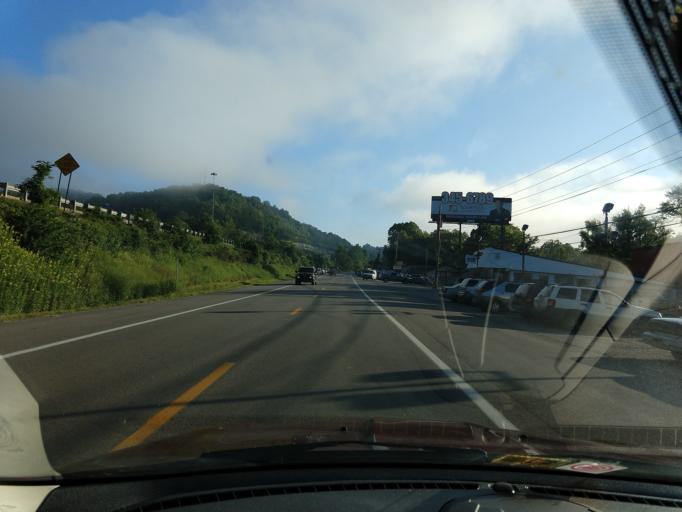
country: US
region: West Virginia
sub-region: Kanawha County
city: Charleston
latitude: 38.3774
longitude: -81.6031
